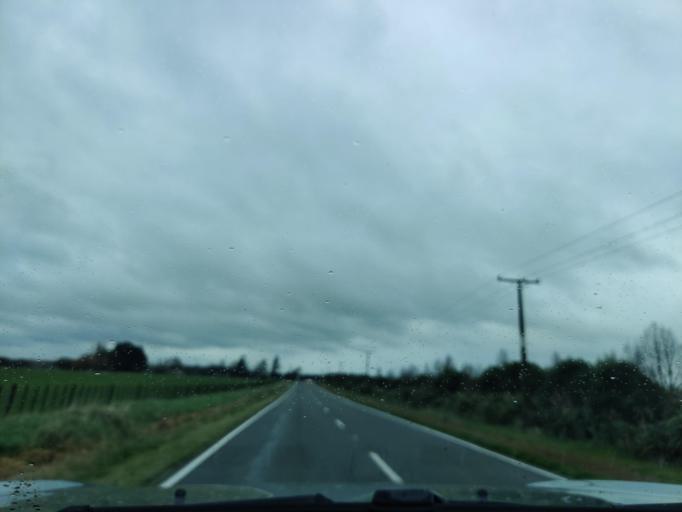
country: NZ
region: Hawke's Bay
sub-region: Hastings District
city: Hastings
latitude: -40.0044
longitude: 176.3918
